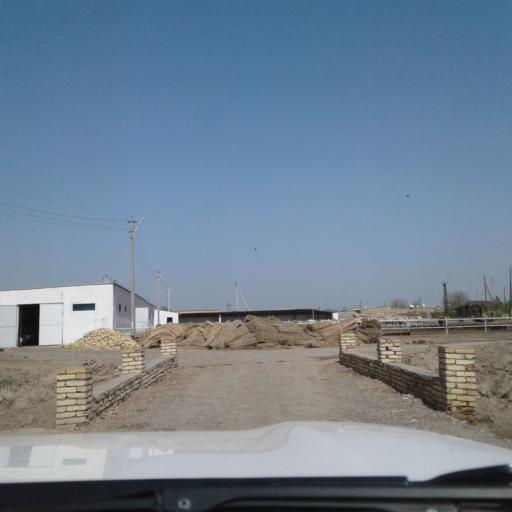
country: TM
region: Lebap
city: Turkmenabat
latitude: 38.9603
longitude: 63.6457
